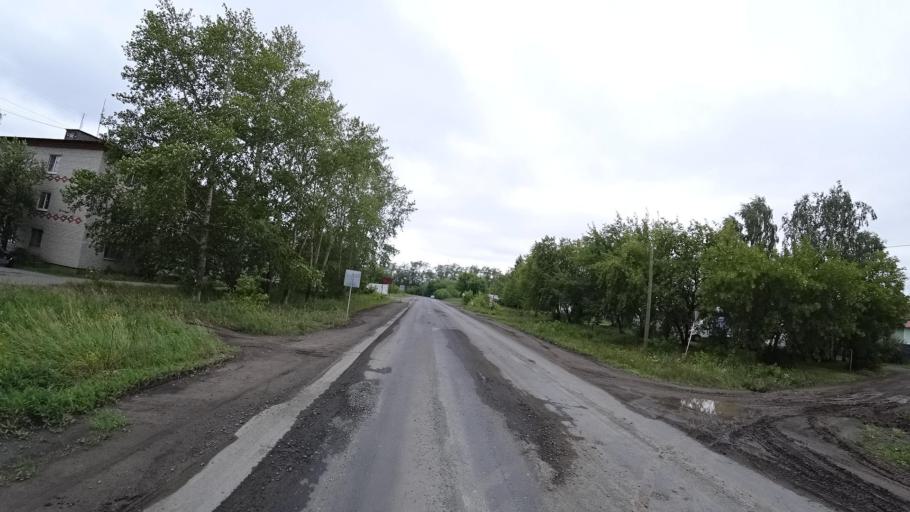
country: RU
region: Sverdlovsk
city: Kamyshlov
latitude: 56.8459
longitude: 62.7581
